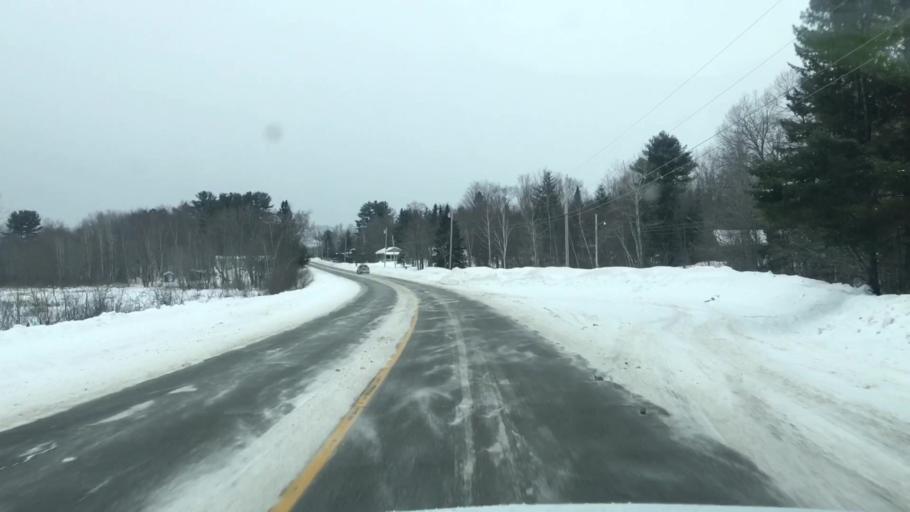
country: US
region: Maine
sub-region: Penobscot County
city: Lincoln
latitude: 45.4046
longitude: -68.4880
